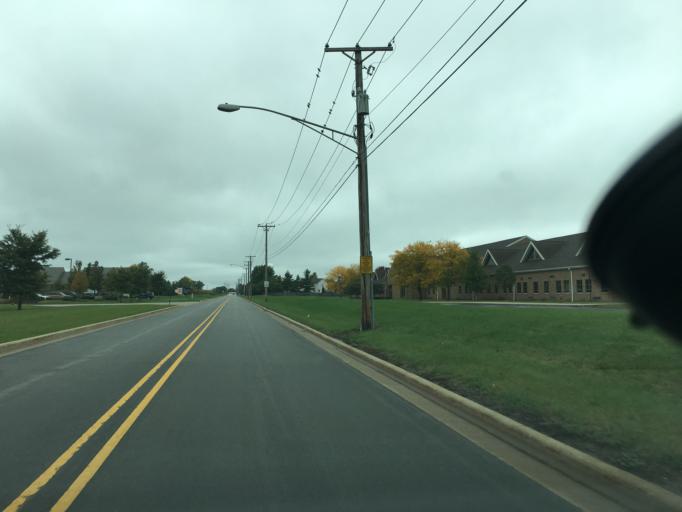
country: US
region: Illinois
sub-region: Will County
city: Plainfield
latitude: 41.6552
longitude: -88.2133
